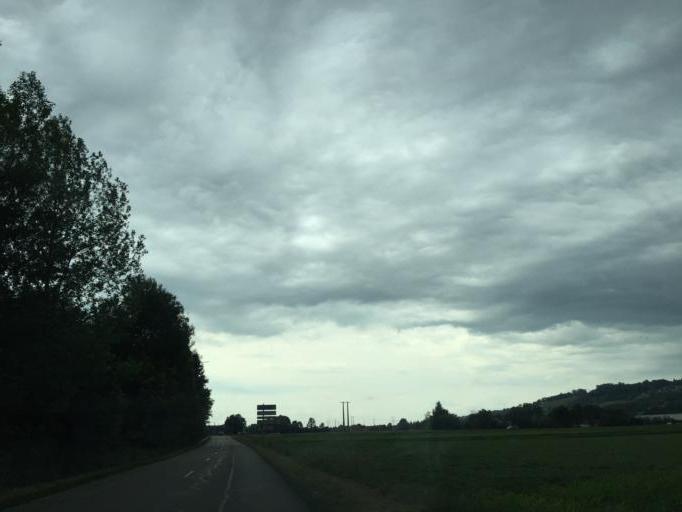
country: FR
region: Rhone-Alpes
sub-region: Departement de la Savoie
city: Le Pont-de-Beauvoisin
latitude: 45.5642
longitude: 5.6696
